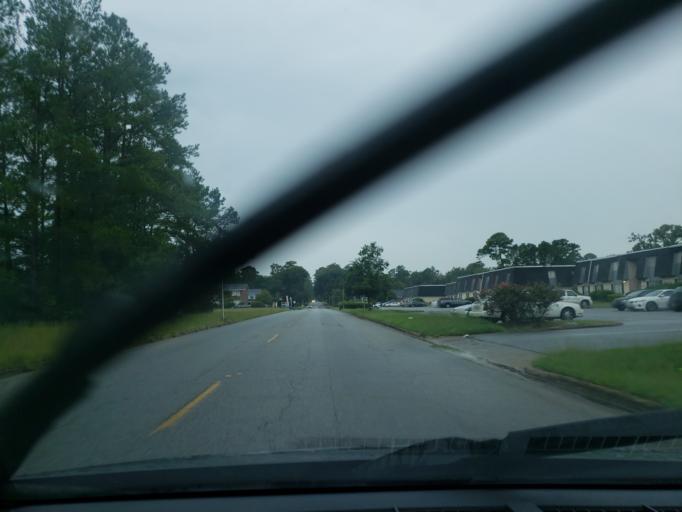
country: US
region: Georgia
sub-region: Dougherty County
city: Albany
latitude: 31.6050
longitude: -84.1817
